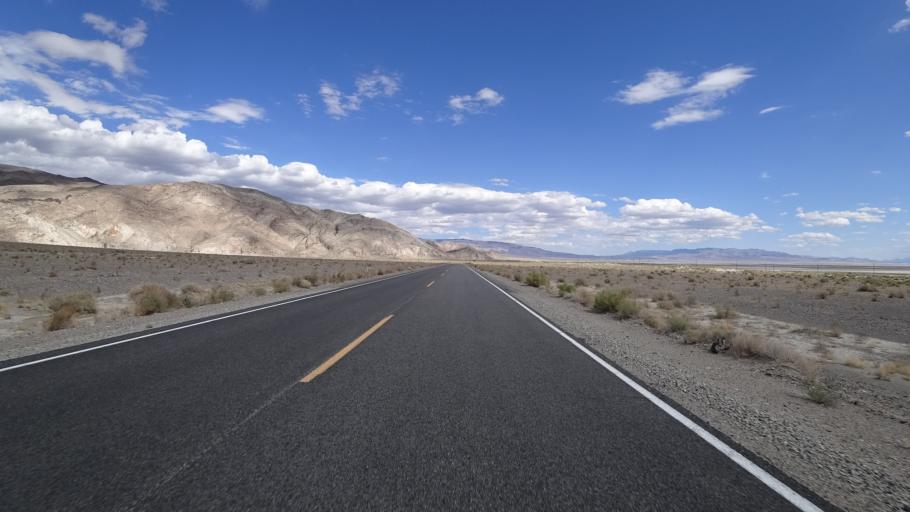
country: US
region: California
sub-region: Inyo County
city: Lone Pine
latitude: 36.5435
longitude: -117.9359
